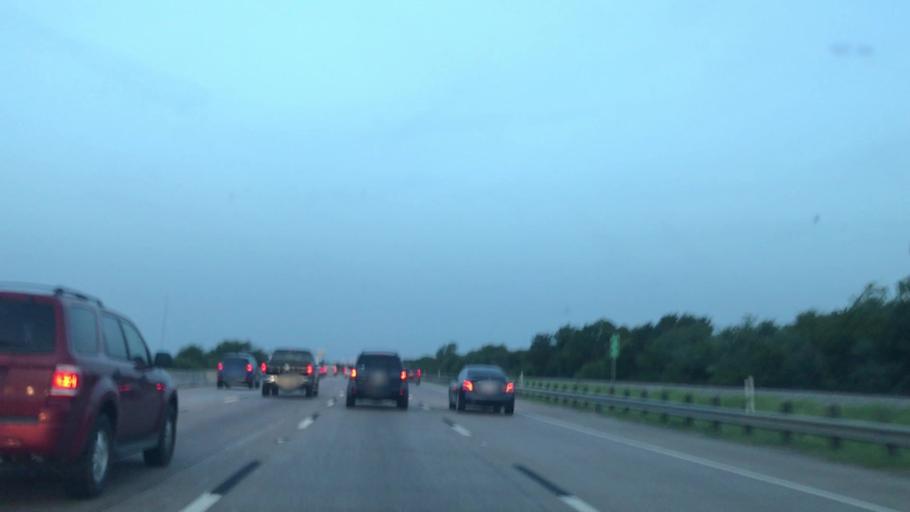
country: US
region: Texas
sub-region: Rockwall County
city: Rockwall
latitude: 32.8889
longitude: -96.4924
